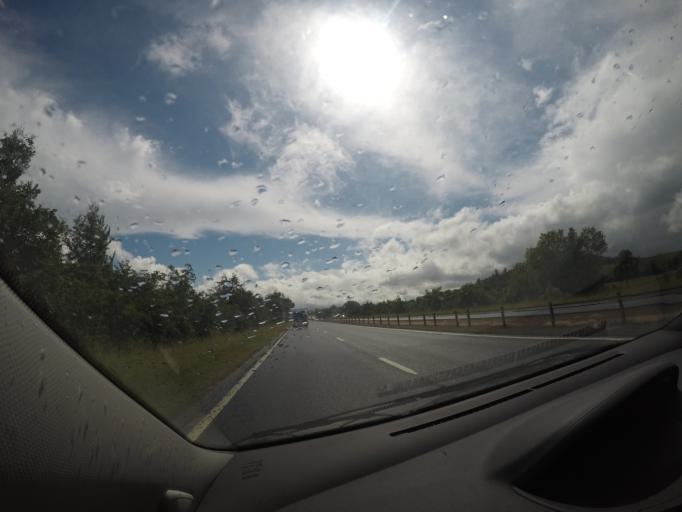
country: GB
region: Scotland
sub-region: Perth and Kinross
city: Auchterarder
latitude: 56.3123
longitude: -3.6599
